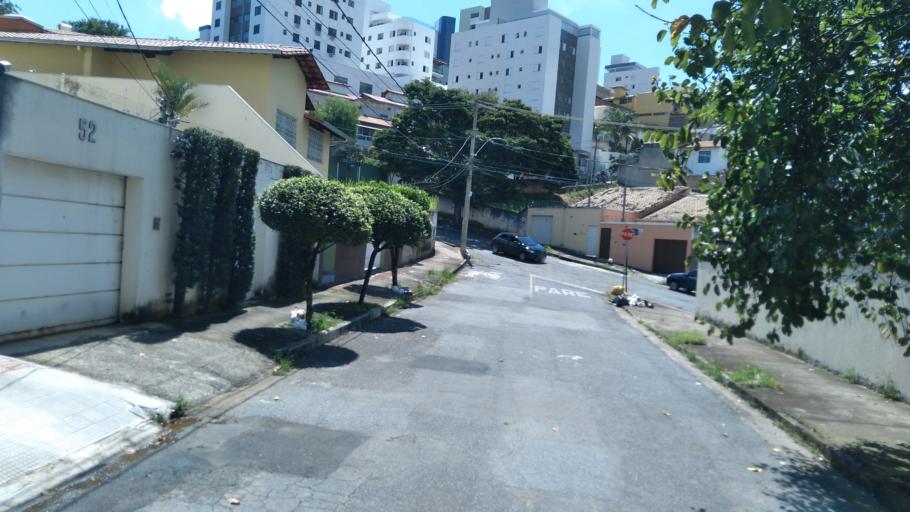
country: BR
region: Minas Gerais
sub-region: Belo Horizonte
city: Belo Horizonte
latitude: -19.8725
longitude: -43.9199
